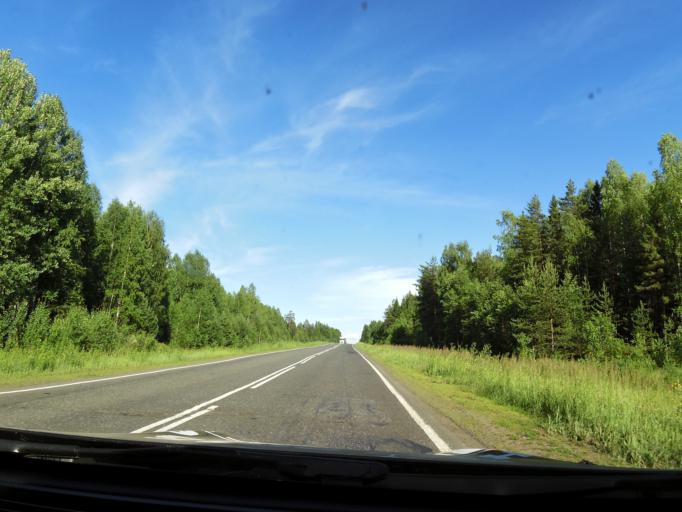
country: RU
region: Kirov
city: Chernaya Kholunitsa
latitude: 58.8878
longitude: 51.3764
